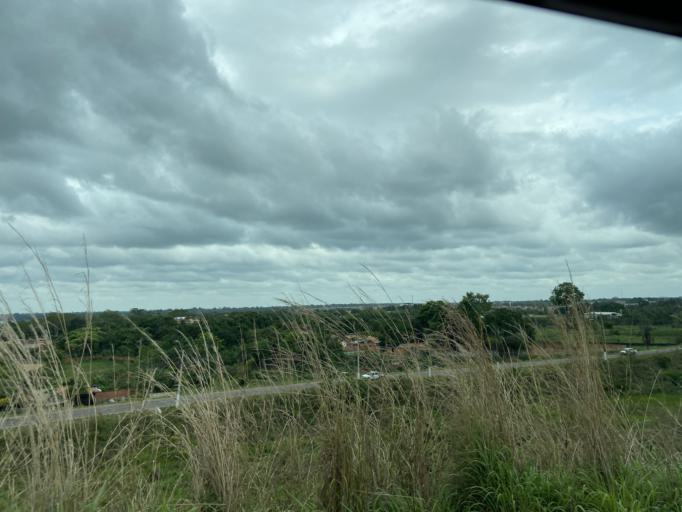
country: BR
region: Para
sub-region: Maraba
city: Maraba
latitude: -5.3043
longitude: -49.0719
